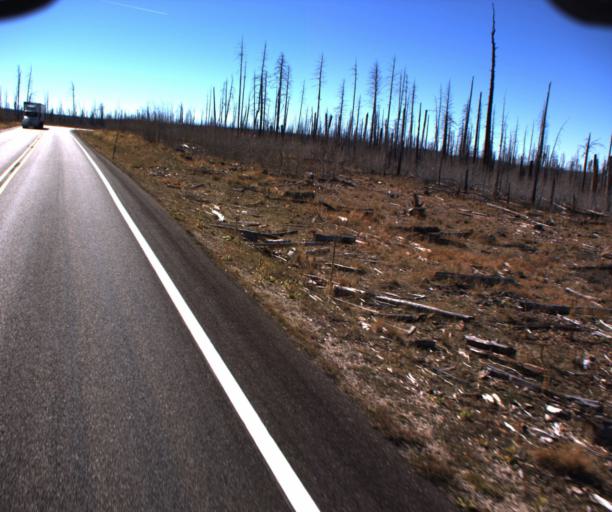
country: US
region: Arizona
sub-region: Coconino County
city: Grand Canyon
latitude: 36.5604
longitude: -112.1711
